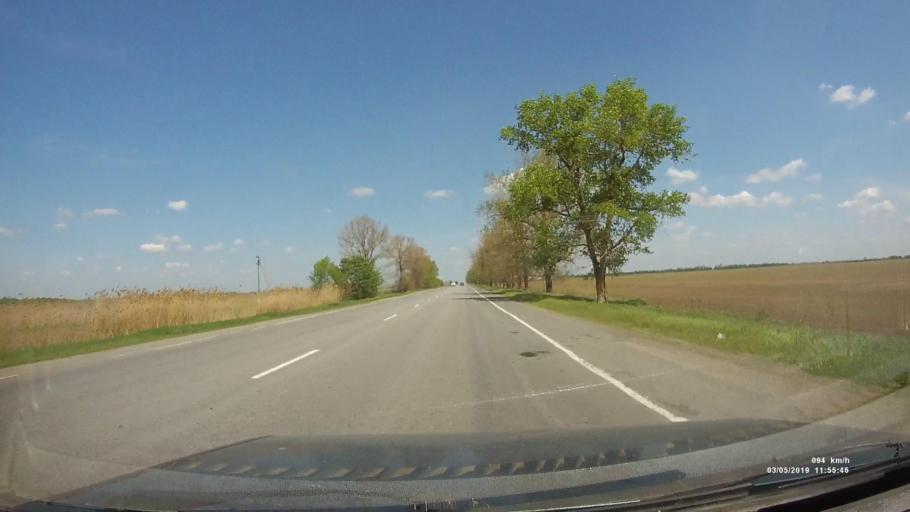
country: RU
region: Rostov
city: Bagayevskaya
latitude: 47.1853
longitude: 40.2942
